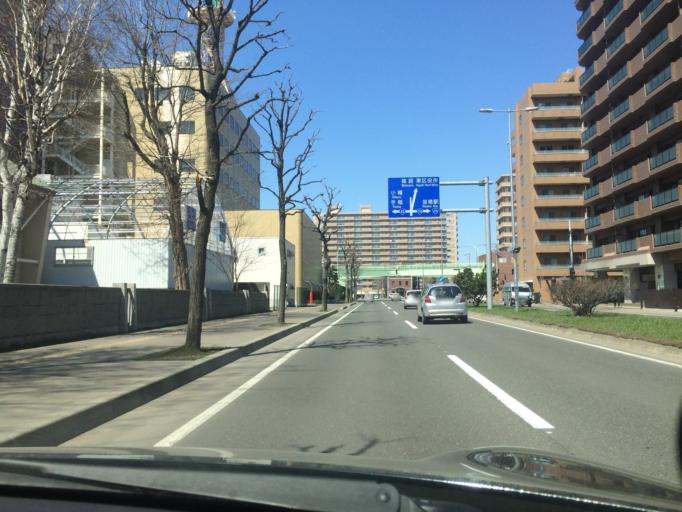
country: JP
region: Hokkaido
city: Sapporo
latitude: 43.0628
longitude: 141.3665
